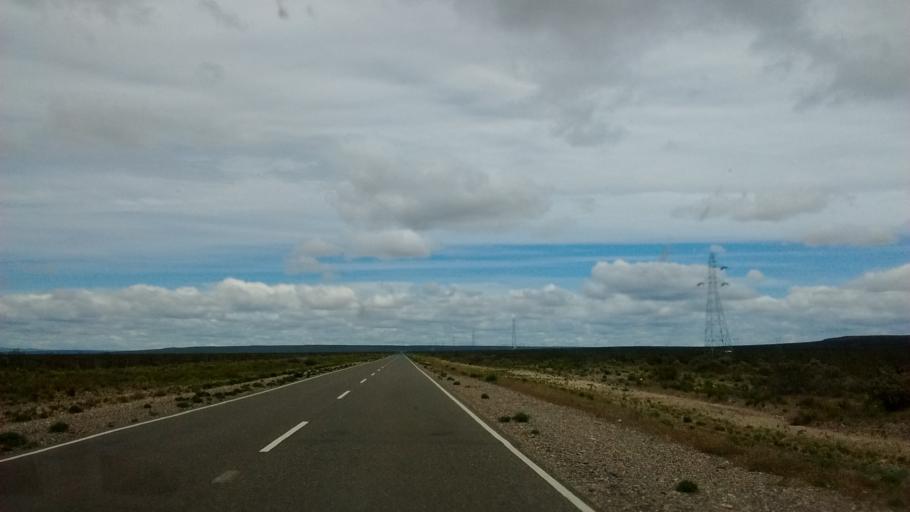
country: AR
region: Neuquen
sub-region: Departamento de Picun Leufu
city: Picun Leufu
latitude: -39.6798
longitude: -69.4591
